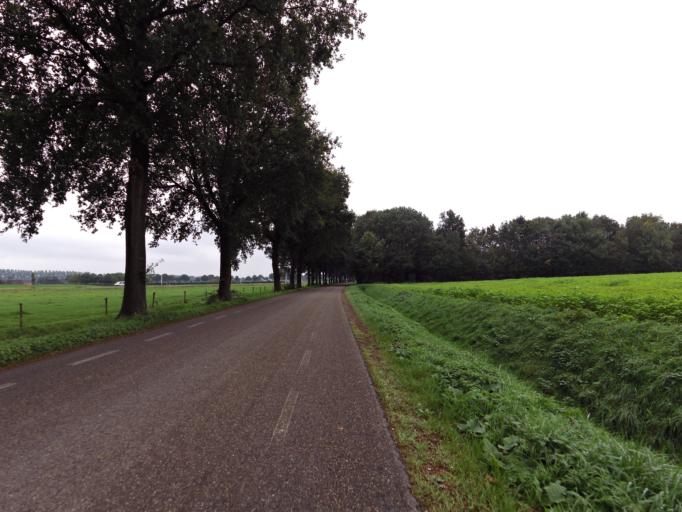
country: NL
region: Gelderland
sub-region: Gemeente Doetinchem
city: Doetinchem
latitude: 51.9307
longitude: 6.3136
